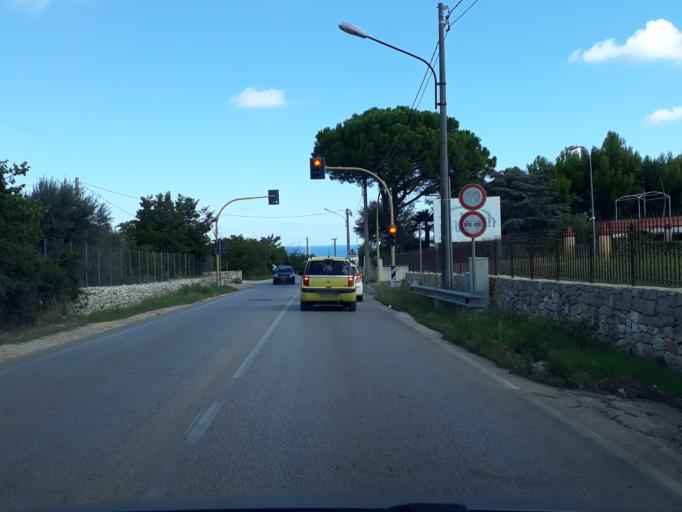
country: IT
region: Apulia
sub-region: Provincia di Bari
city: Mola di Bari
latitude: 41.0374
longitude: 17.0488
